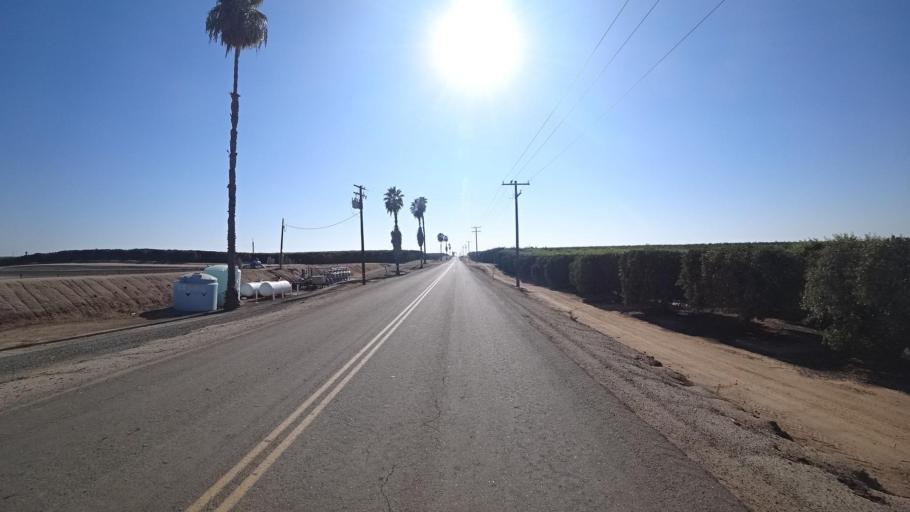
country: US
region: California
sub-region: Tulare County
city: Richgrove
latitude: 35.7155
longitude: -119.1339
